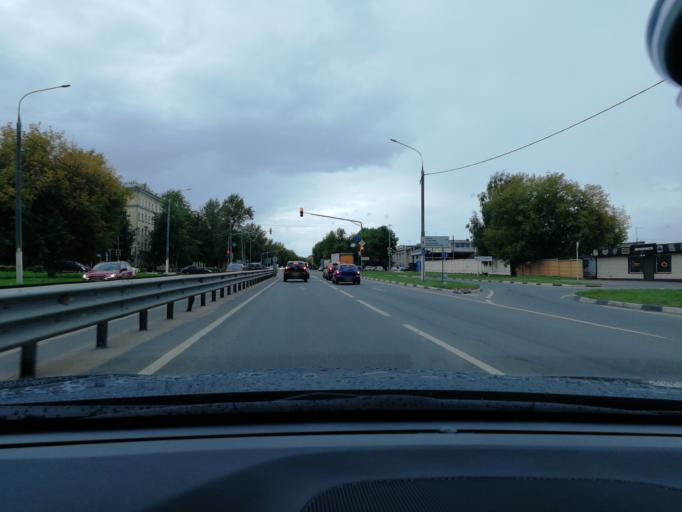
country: RU
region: Moskovskaya
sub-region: Podol'skiy Rayon
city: Podol'sk
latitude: 55.4138
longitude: 37.5493
